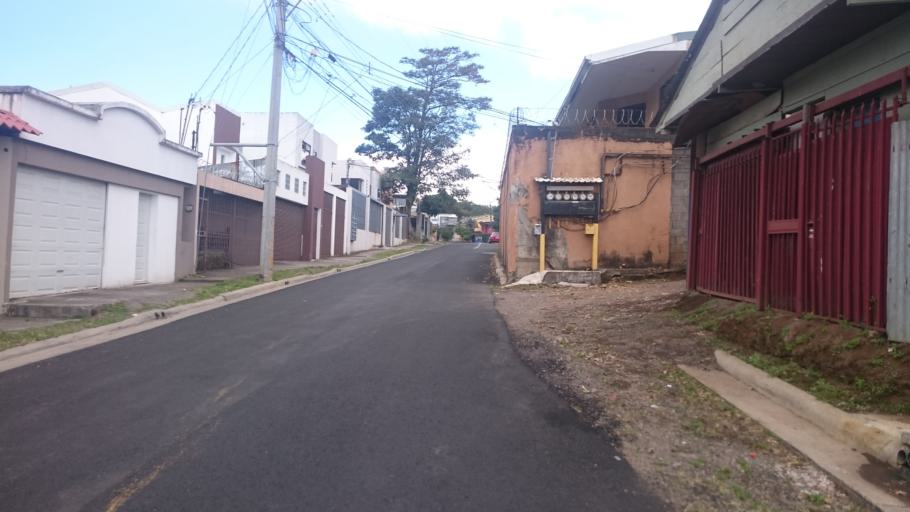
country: CR
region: San Jose
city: Curridabat
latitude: 9.9219
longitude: -84.0281
